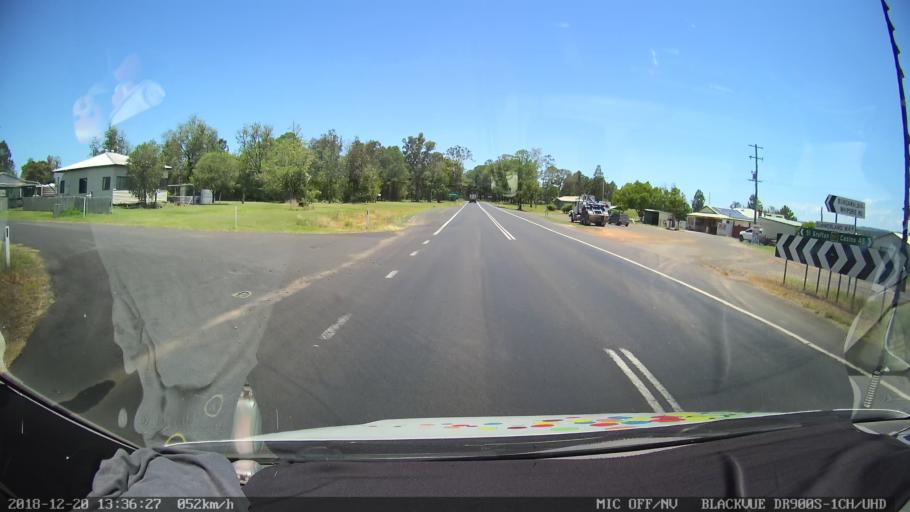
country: AU
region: New South Wales
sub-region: Clarence Valley
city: Maclean
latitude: -29.2818
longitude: 152.9896
